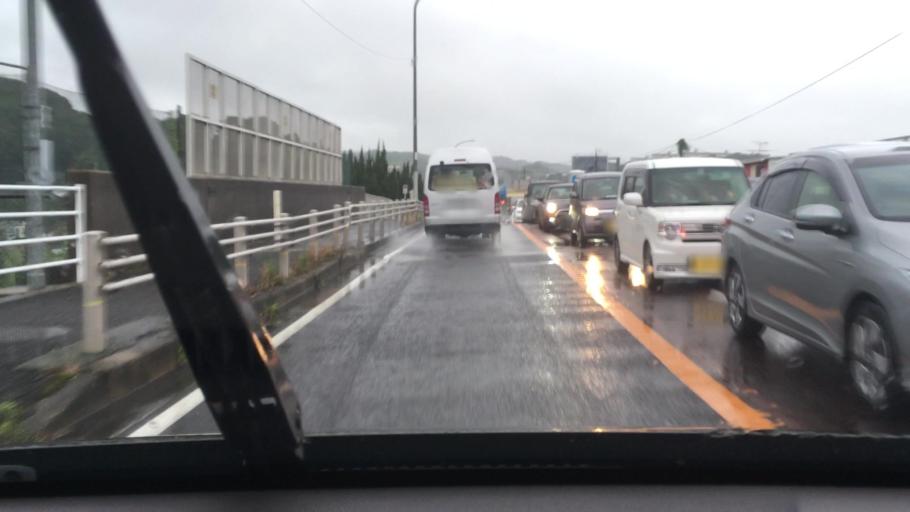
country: JP
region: Nagasaki
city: Sasebo
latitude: 33.1412
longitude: 129.7969
